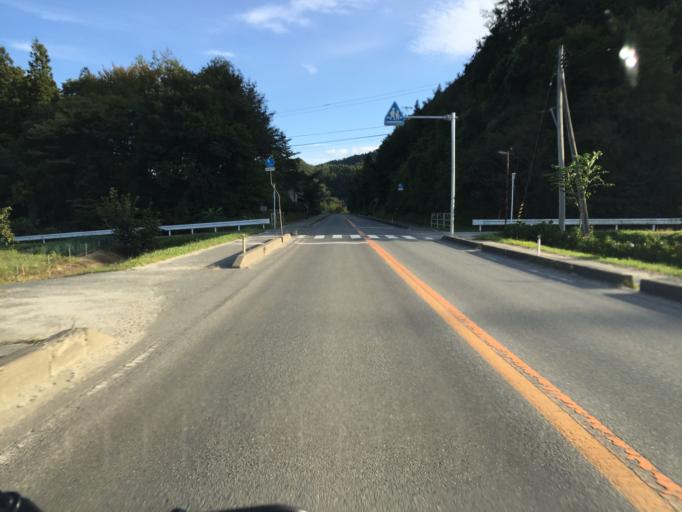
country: JP
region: Fukushima
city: Hobaramachi
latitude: 37.6955
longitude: 140.6084
